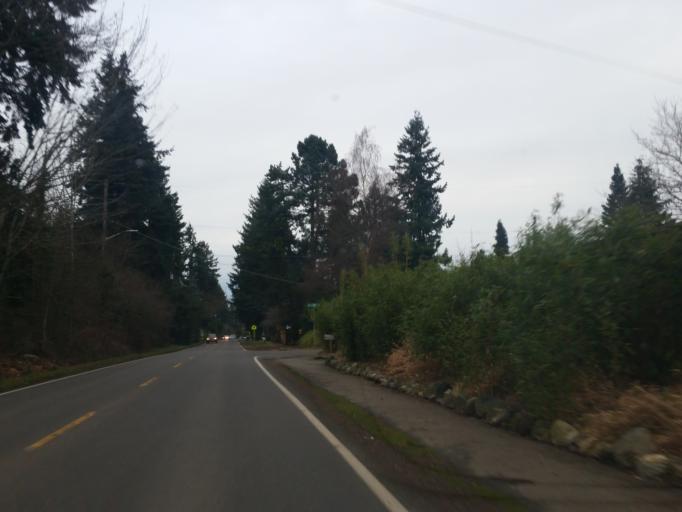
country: US
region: Washington
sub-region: King County
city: Shoreline
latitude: 47.7269
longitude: -122.3609
